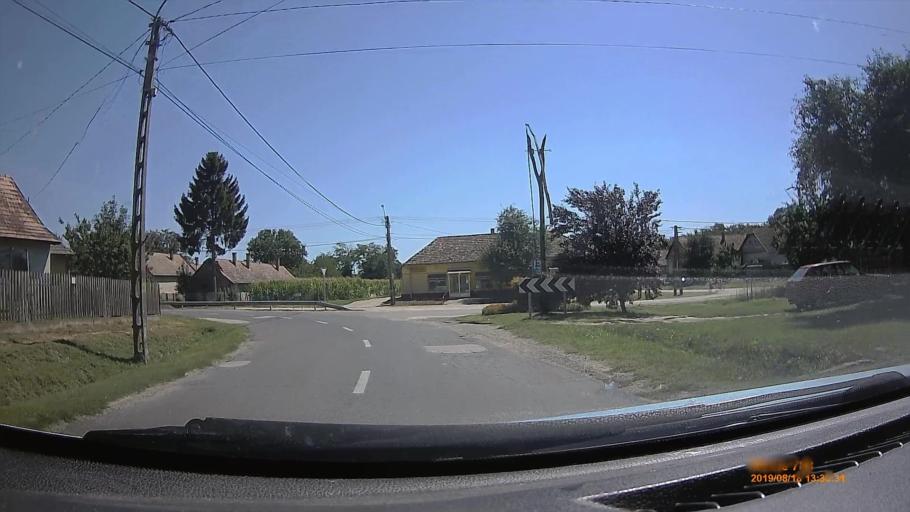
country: HU
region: Fejer
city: Cece
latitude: 46.7812
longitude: 18.5927
